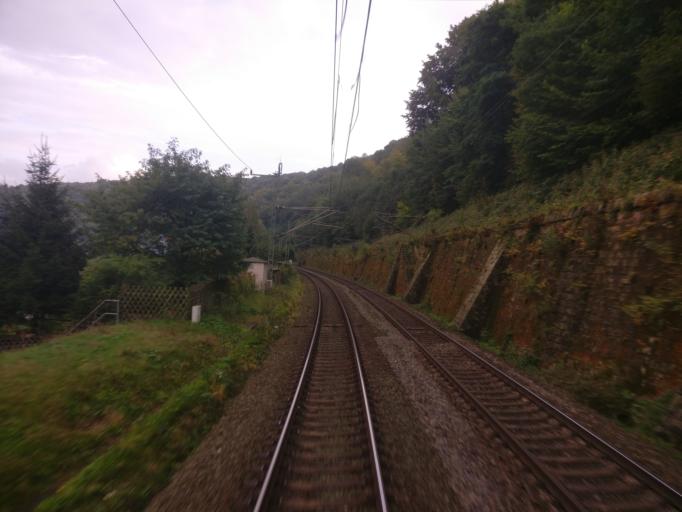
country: DE
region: Saxony
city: Struppen
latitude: 50.9448
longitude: 14.0007
